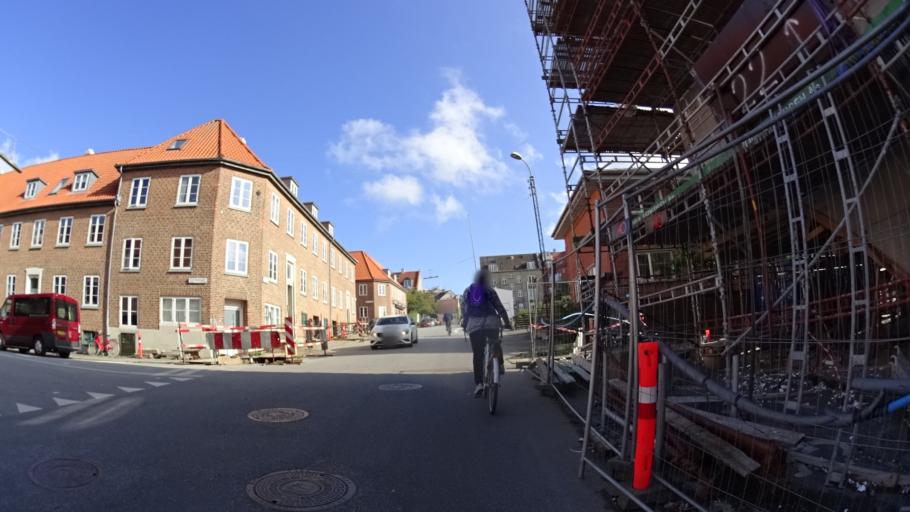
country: DK
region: Central Jutland
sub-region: Arhus Kommune
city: Arhus
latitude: 56.1502
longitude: 10.1952
